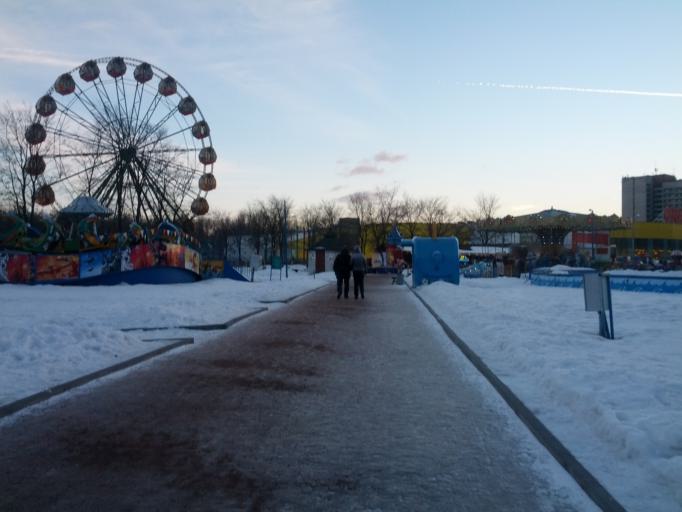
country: RU
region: St.-Petersburg
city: Krasnogvargeisky
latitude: 59.9139
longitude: 30.4820
